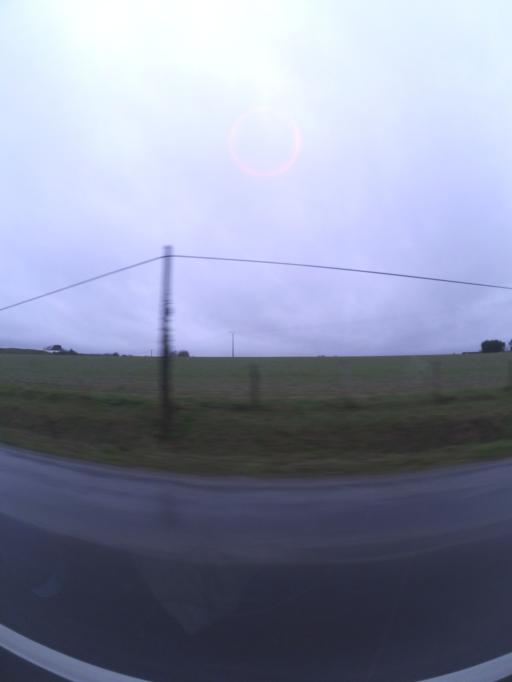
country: FR
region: Pays de la Loire
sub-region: Departement de la Loire-Atlantique
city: Vieillevigne
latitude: 46.9809
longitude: -1.4397
